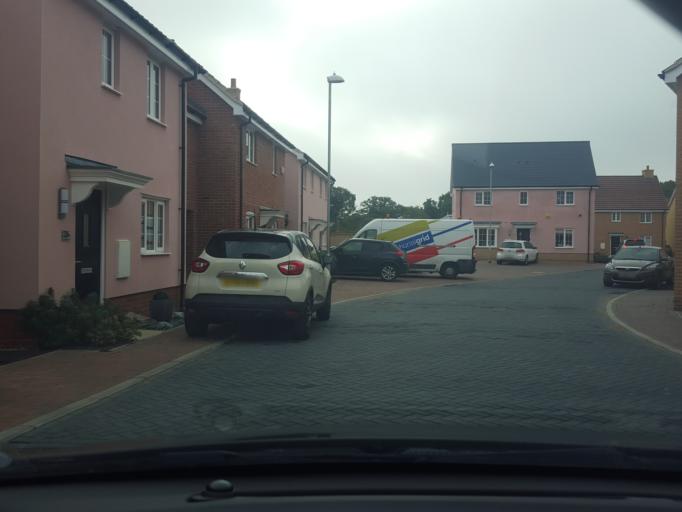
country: GB
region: England
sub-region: Essex
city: Little Clacton
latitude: 51.8052
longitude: 1.1262
